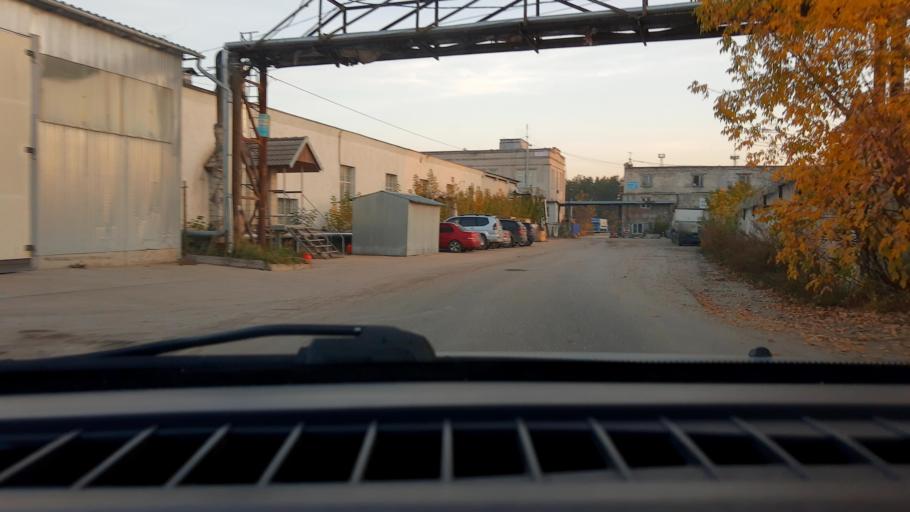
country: RU
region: Nizjnij Novgorod
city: Gorbatovka
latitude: 56.3751
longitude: 43.7883
